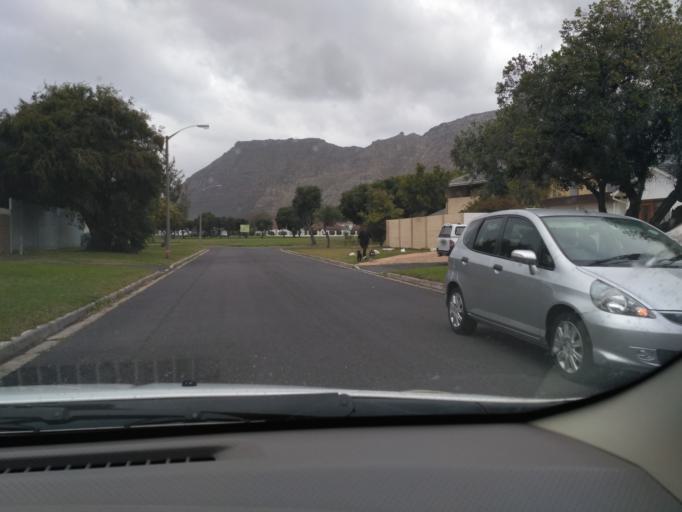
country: ZA
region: Western Cape
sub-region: City of Cape Town
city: Bergvliet
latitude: -34.0708
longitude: 18.4527
